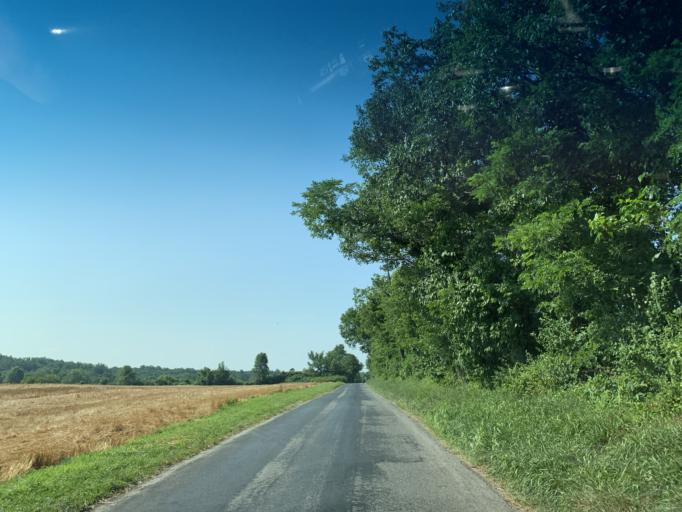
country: US
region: Maryland
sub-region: Montgomery County
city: Poolesville
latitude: 39.1383
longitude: -77.4504
